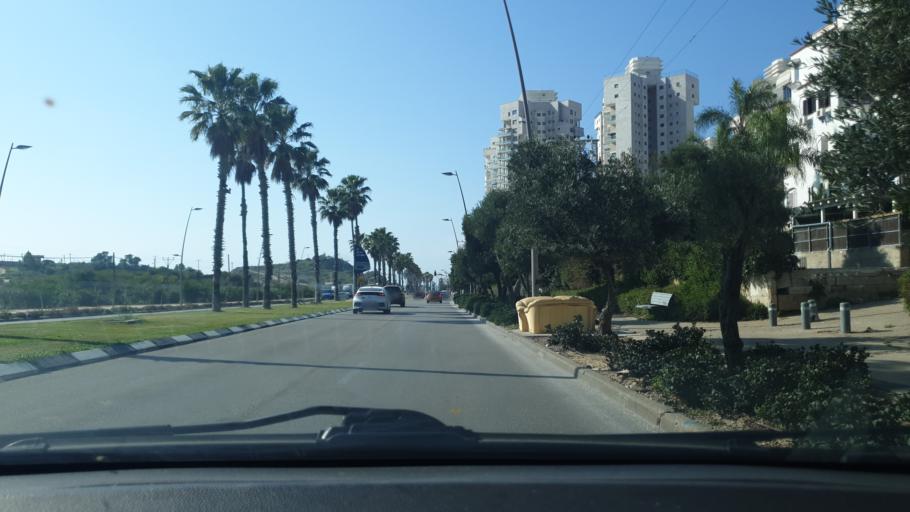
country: IL
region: Tel Aviv
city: Bat Yam
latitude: 31.9951
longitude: 34.7390
